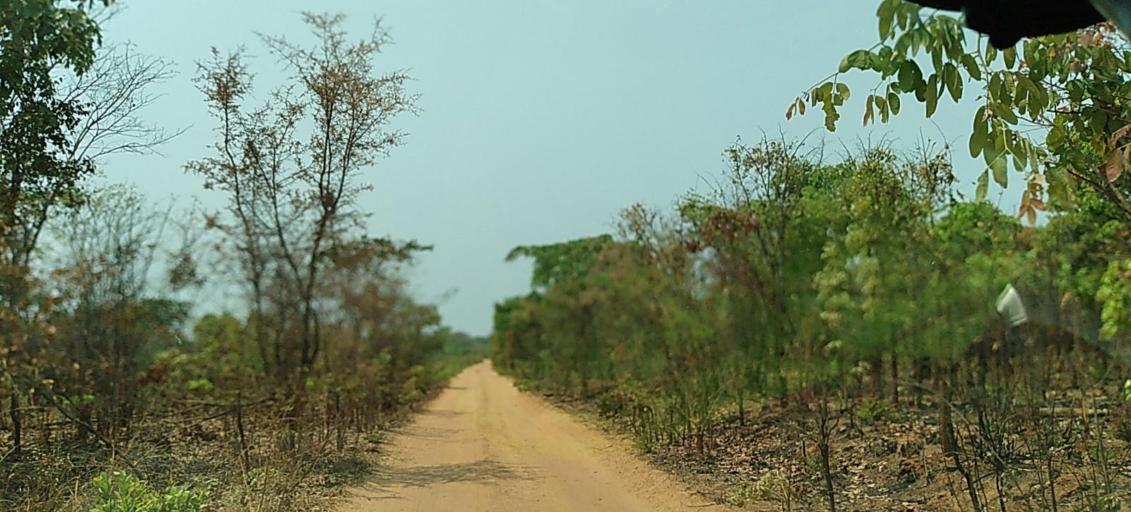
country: ZM
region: North-Western
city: Kabompo
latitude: -13.6961
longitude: 24.3127
